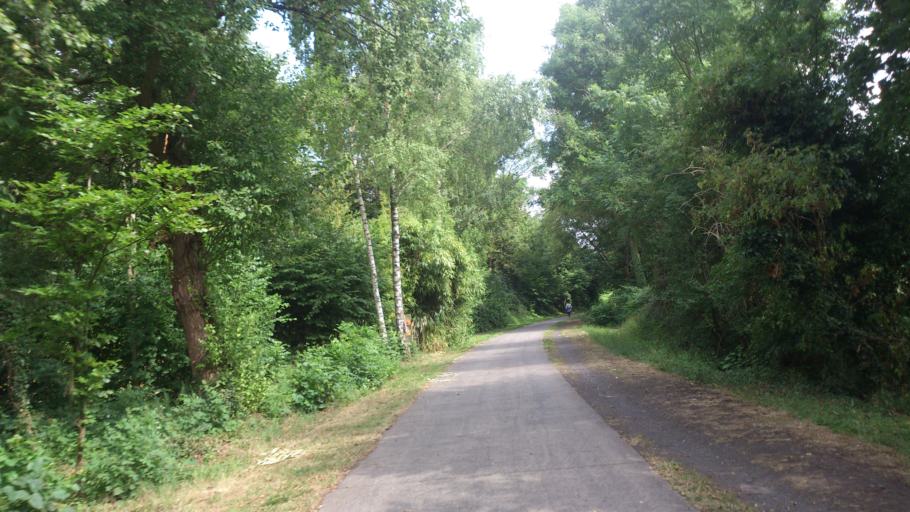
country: BE
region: Wallonia
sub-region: Province de Liege
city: Beyne-Heusay
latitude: 50.6238
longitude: 5.6482
